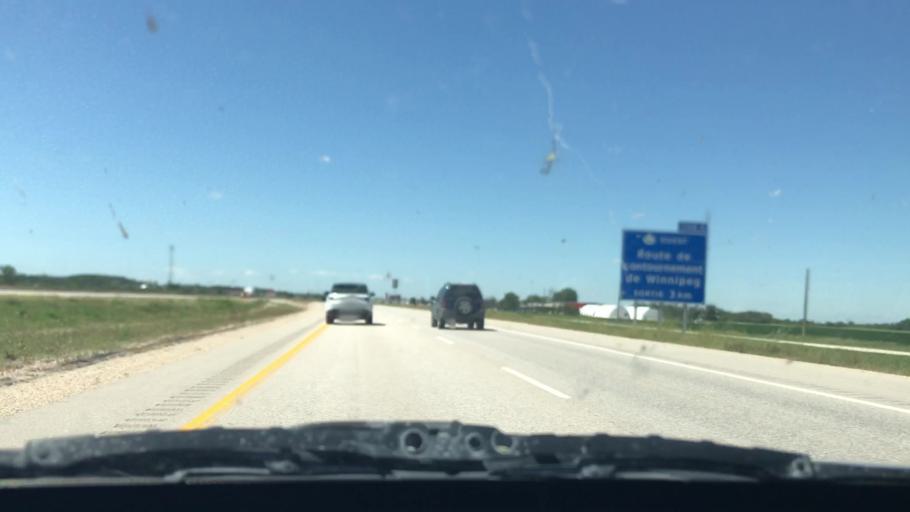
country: CA
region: Manitoba
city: Winnipeg
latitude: 49.8169
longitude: -96.9270
